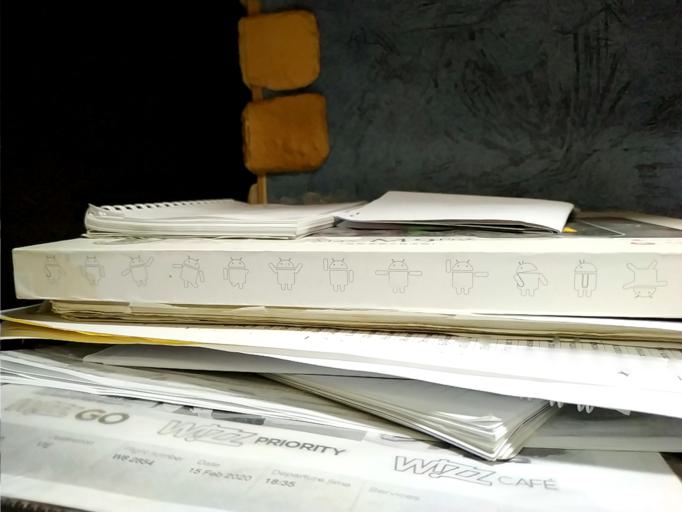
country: RU
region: Arkhangelskaya
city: Onega
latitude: 63.1064
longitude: 38.3774
